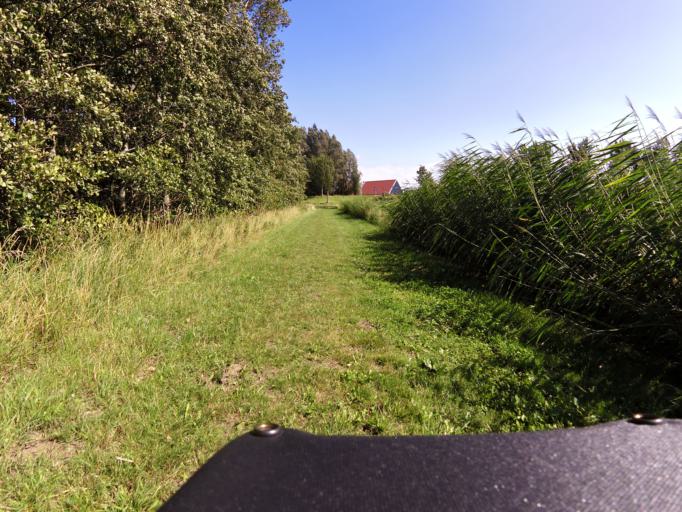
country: NL
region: South Holland
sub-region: Gemeente Goeree-Overflakkee
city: Dirksland
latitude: 51.7640
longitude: 4.0678
